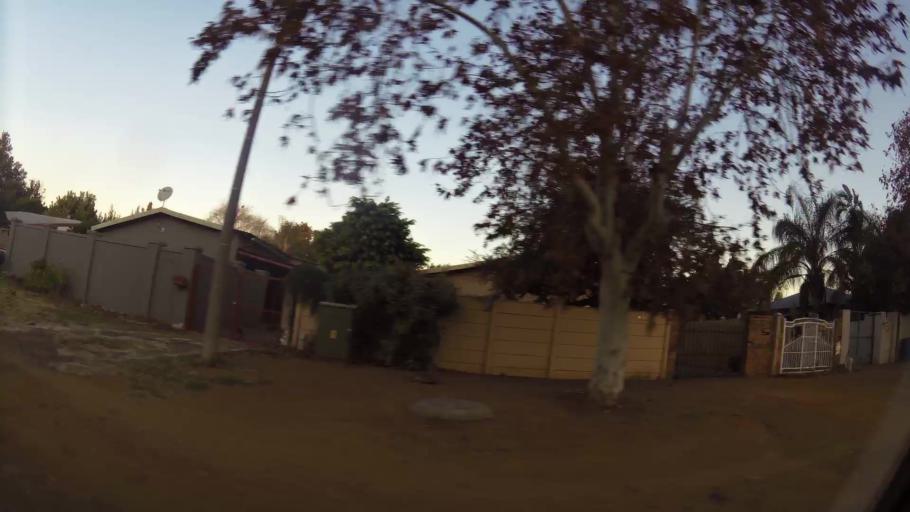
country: ZA
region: North-West
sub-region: Bojanala Platinum District Municipality
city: Rustenburg
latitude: -25.6706
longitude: 27.2268
